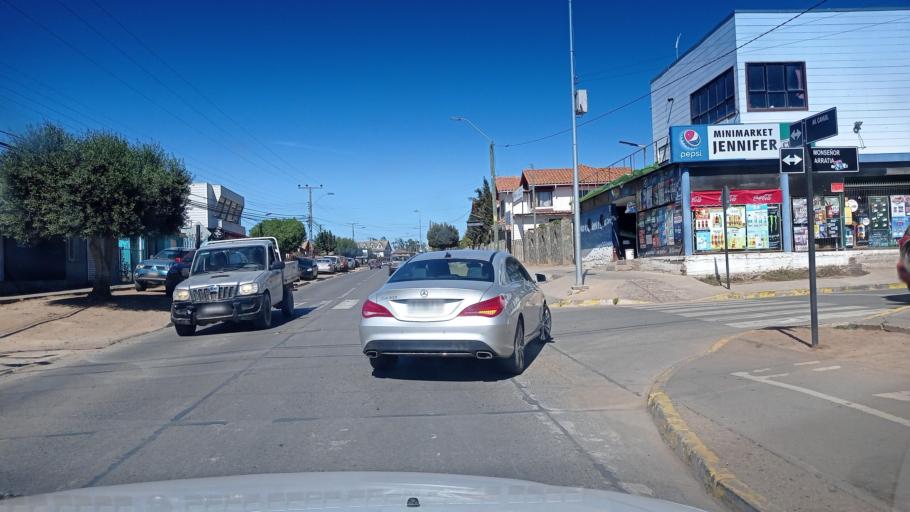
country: CL
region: O'Higgins
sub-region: Provincia de Colchagua
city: Santa Cruz
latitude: -34.3888
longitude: -71.9968
